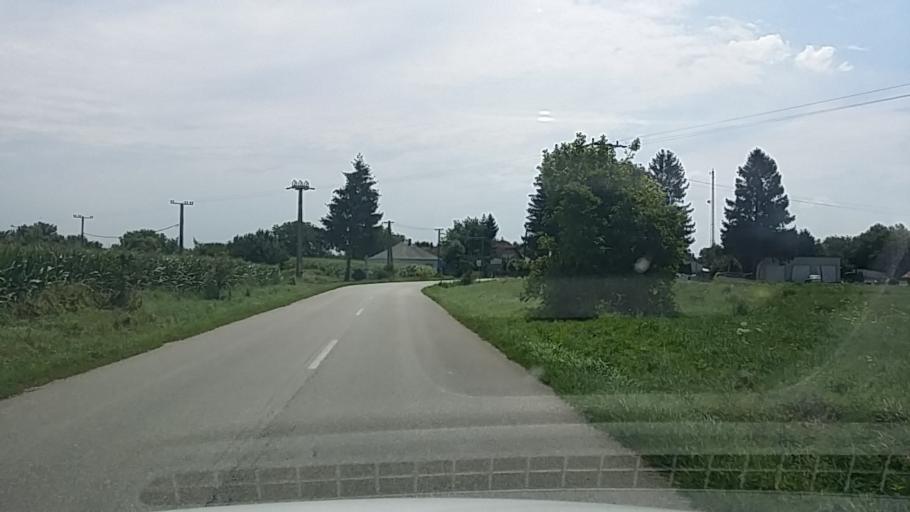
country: HU
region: Zala
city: Becsehely
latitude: 46.4047
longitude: 16.7880
